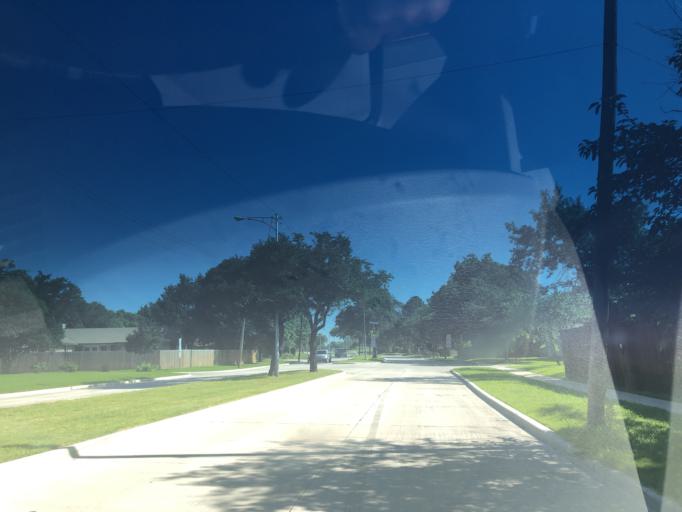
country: US
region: Texas
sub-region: Dallas County
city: Grand Prairie
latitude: 32.7145
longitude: -97.0151
